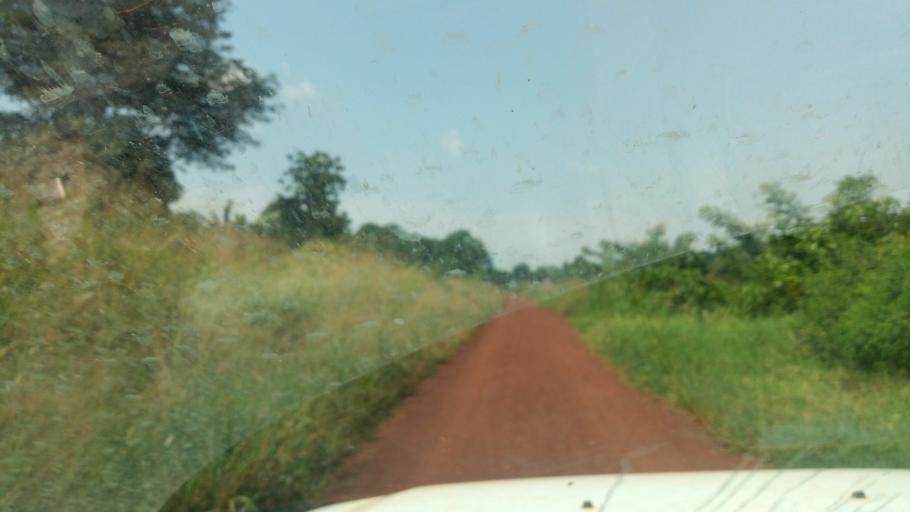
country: UG
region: Western Region
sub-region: Masindi District
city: Masindi
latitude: 1.6451
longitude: 31.8052
